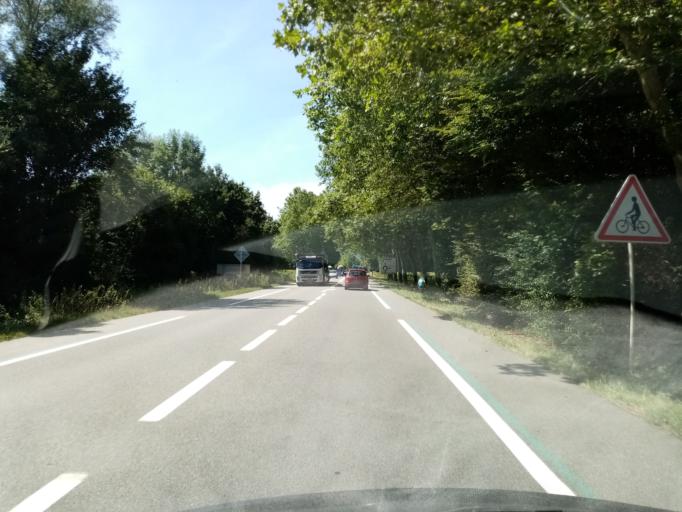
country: FR
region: Alsace
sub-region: Departement du Bas-Rhin
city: Selestat
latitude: 48.2451
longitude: 7.4630
